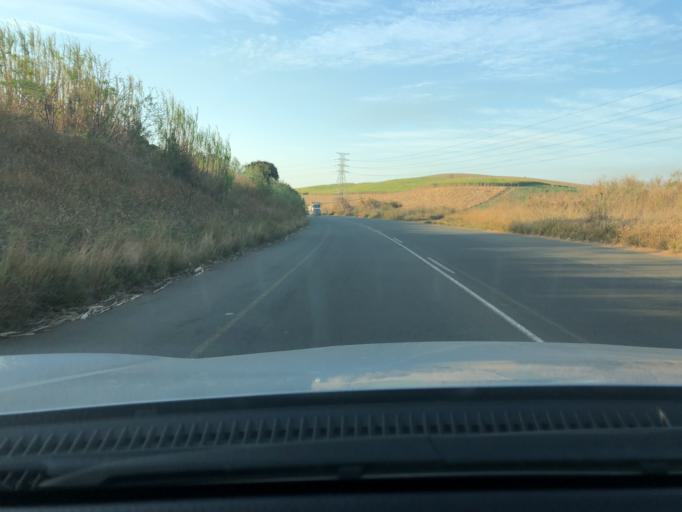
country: ZA
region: KwaZulu-Natal
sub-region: iLembe District Municipality
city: Ballitoville
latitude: -29.6050
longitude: 31.0940
